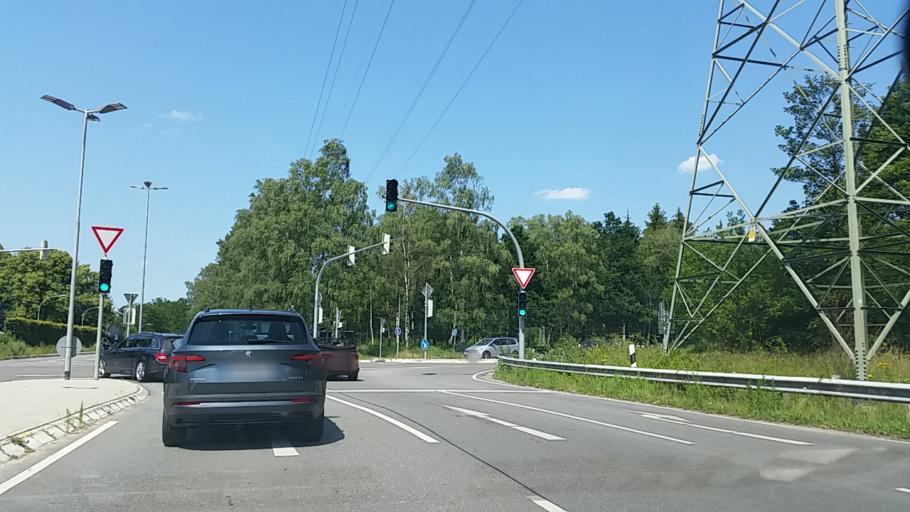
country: DE
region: Schleswig-Holstein
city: Reinbek
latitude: 53.5524
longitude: 10.2523
